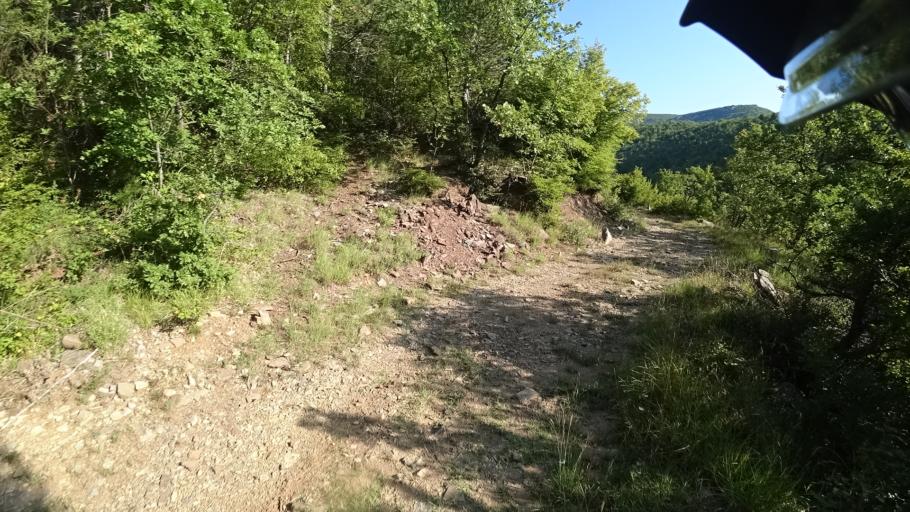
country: HR
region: Sibensko-Kniniska
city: Knin
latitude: 44.1105
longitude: 16.2094
